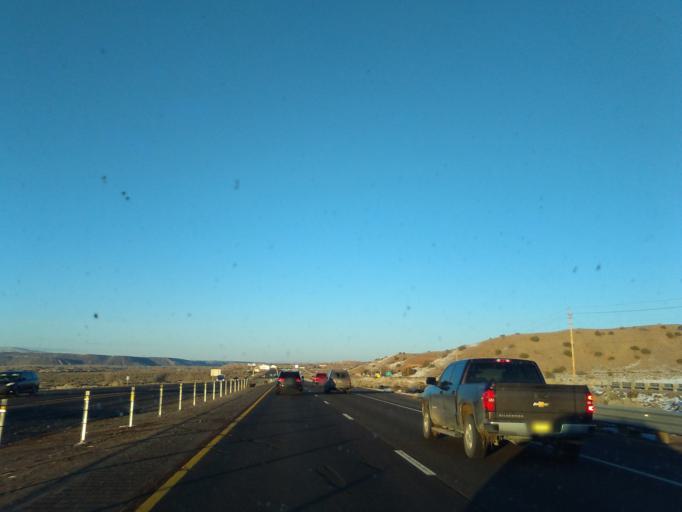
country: US
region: New Mexico
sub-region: Sandoval County
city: Bernalillo
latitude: 35.3300
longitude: -106.5248
